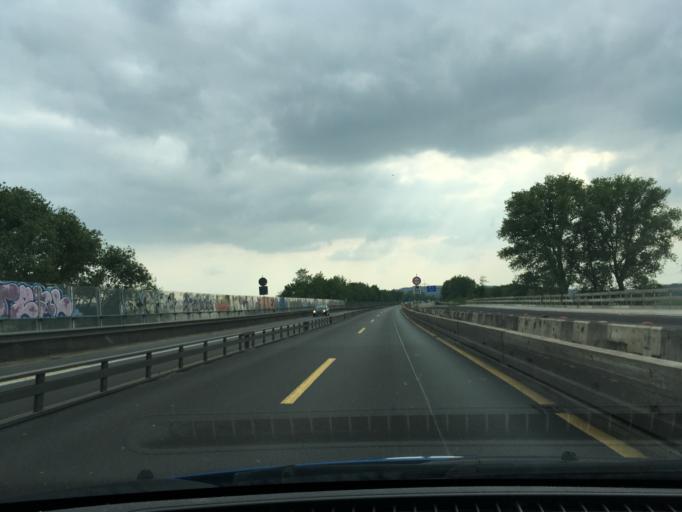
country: DE
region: North Rhine-Westphalia
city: Loehne
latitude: 52.1963
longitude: 8.6855
